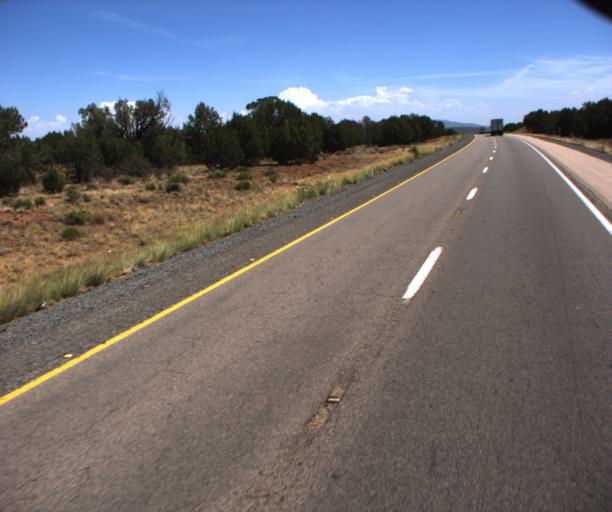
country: US
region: Arizona
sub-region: Mohave County
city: Peach Springs
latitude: 35.2099
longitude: -113.2652
